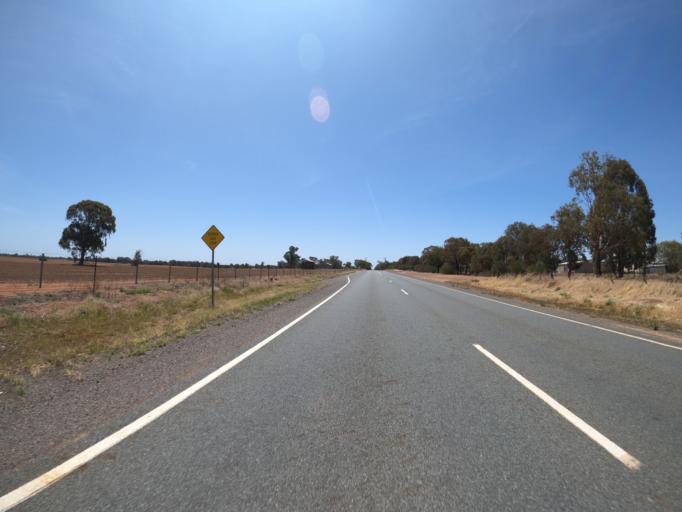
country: AU
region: Victoria
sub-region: Moira
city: Yarrawonga
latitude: -36.0499
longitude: 145.9955
